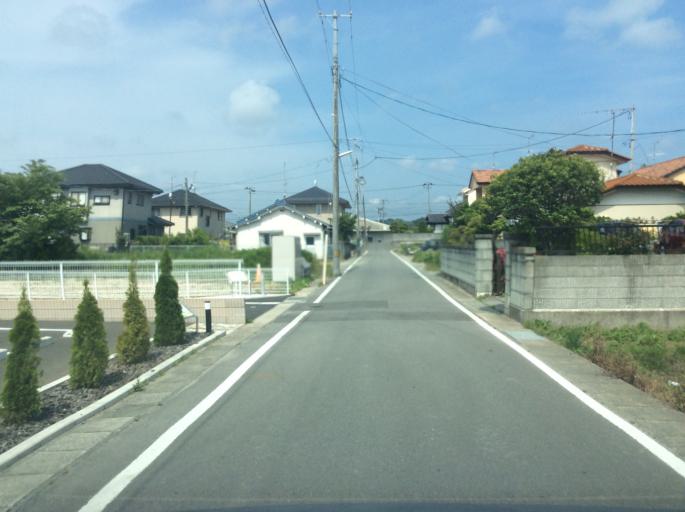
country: JP
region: Fukushima
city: Iwaki
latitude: 37.0678
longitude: 140.9511
